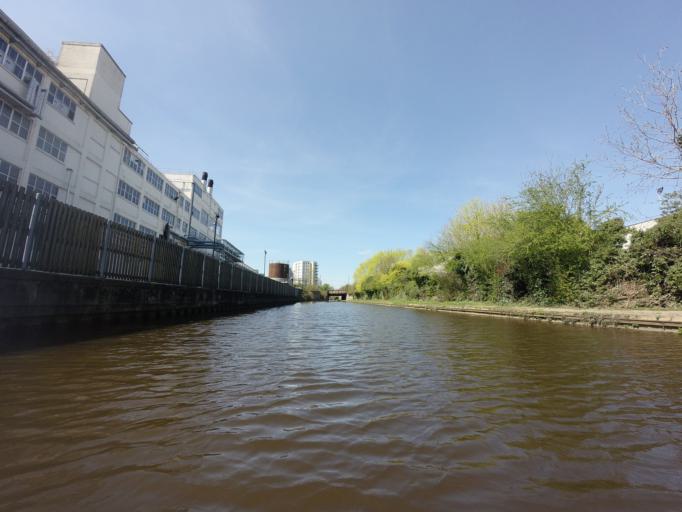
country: GB
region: England
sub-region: Greater London
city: Hayes
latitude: 51.5018
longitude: -0.4133
